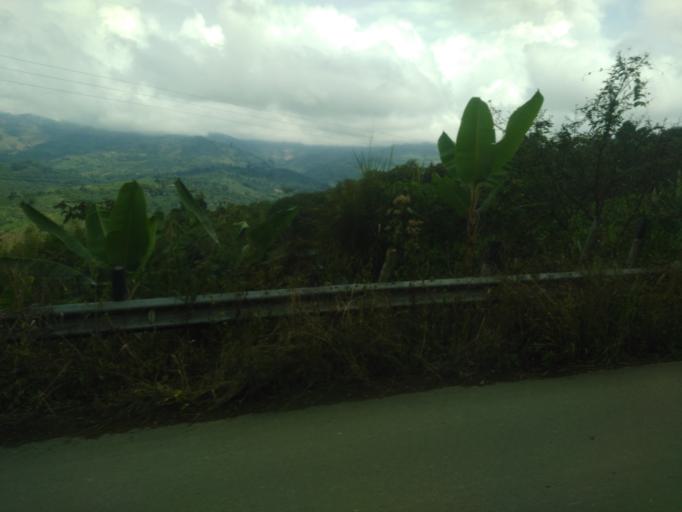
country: CO
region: Valle del Cauca
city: Sevilla
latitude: 4.2959
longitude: -75.8998
